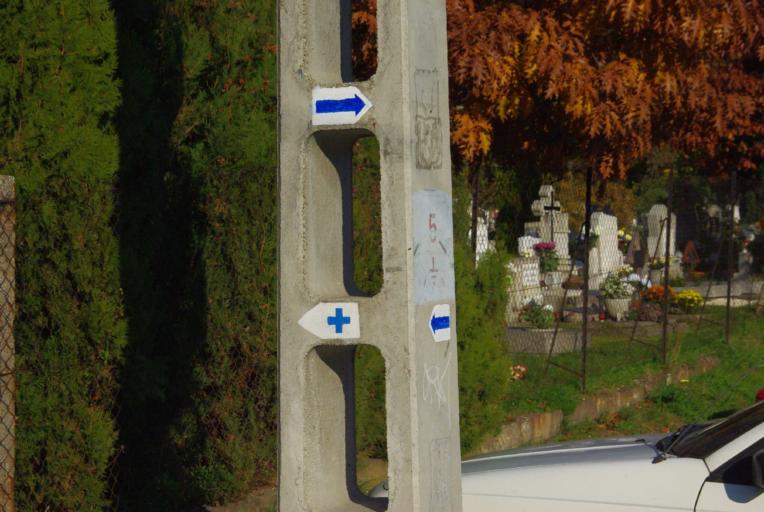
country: HU
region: Pest
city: Piliscsaba
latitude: 47.6338
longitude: 18.8311
